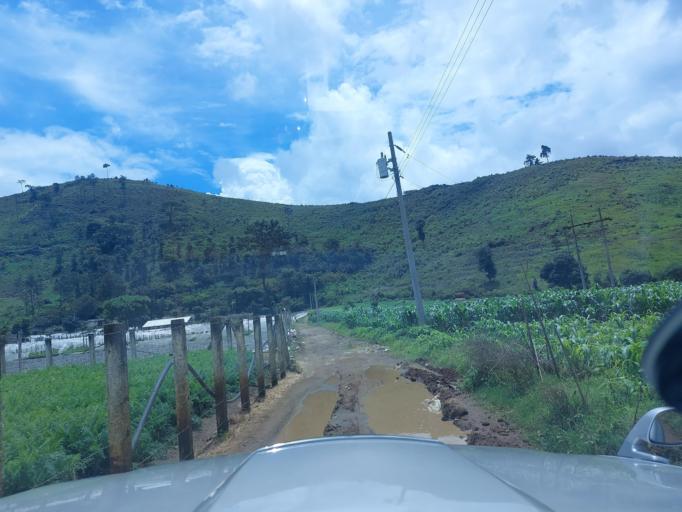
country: GT
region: Chimaltenango
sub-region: Municipio de Chimaltenango
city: Chimaltenango
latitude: 14.6464
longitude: -90.8262
